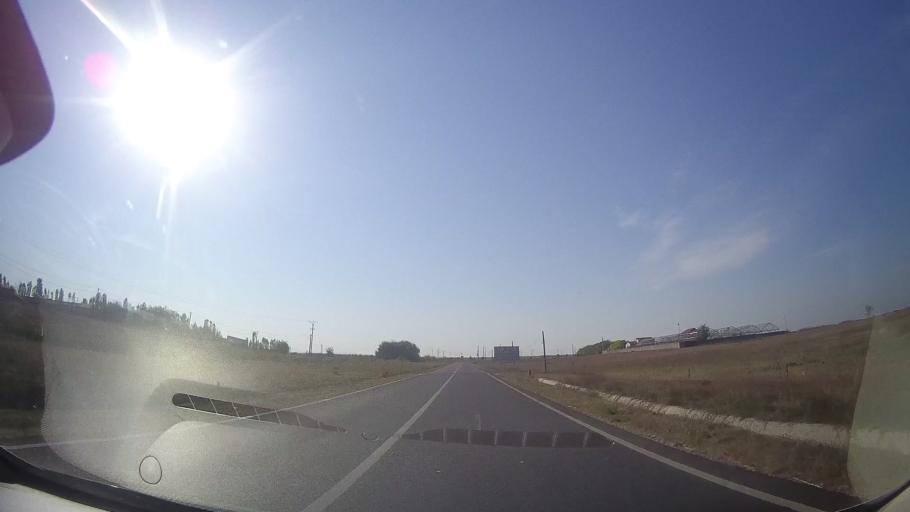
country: RO
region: Timis
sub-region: Oras Recas
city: Recas
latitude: 45.8099
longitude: 21.5287
